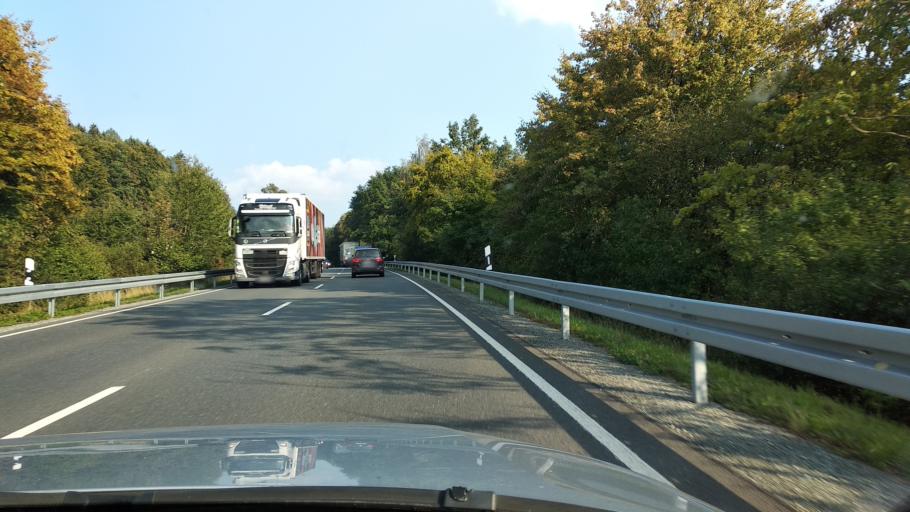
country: DE
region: Bavaria
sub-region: Upper Bavaria
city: Amerang
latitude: 48.0400
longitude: 12.2977
